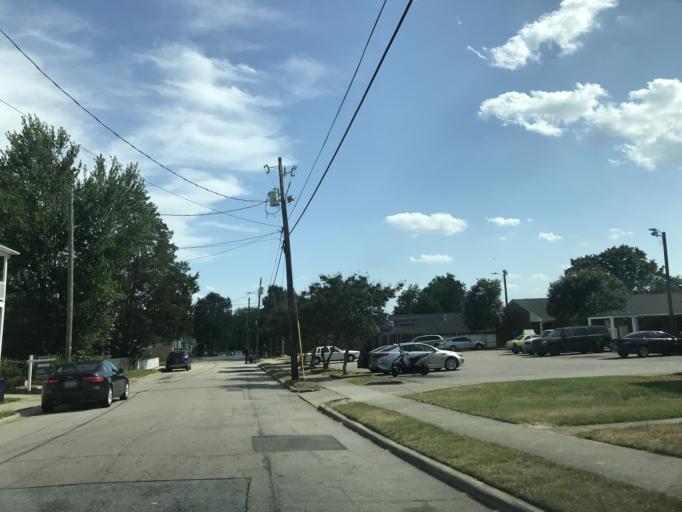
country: US
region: North Carolina
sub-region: Wake County
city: Raleigh
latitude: 35.7776
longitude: -78.6264
